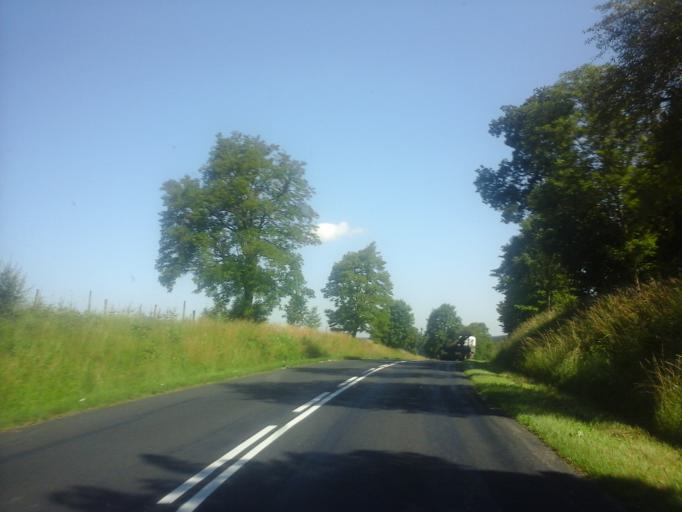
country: PL
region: West Pomeranian Voivodeship
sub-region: Powiat swidwinski
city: Polczyn-Zdroj
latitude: 53.8809
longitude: 16.0684
